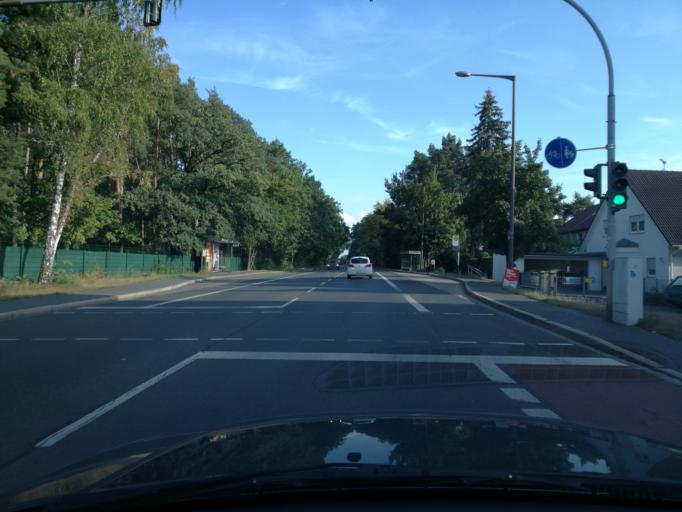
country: DE
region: Bavaria
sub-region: Regierungsbezirk Mittelfranken
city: Furth
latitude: 49.4991
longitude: 10.9839
